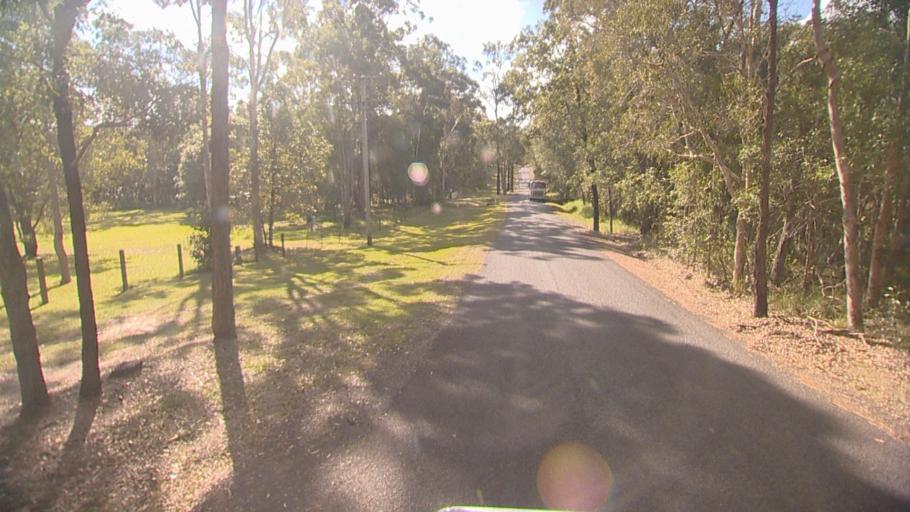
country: AU
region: Queensland
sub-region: Logan
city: Beenleigh
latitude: -27.6499
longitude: 153.2279
